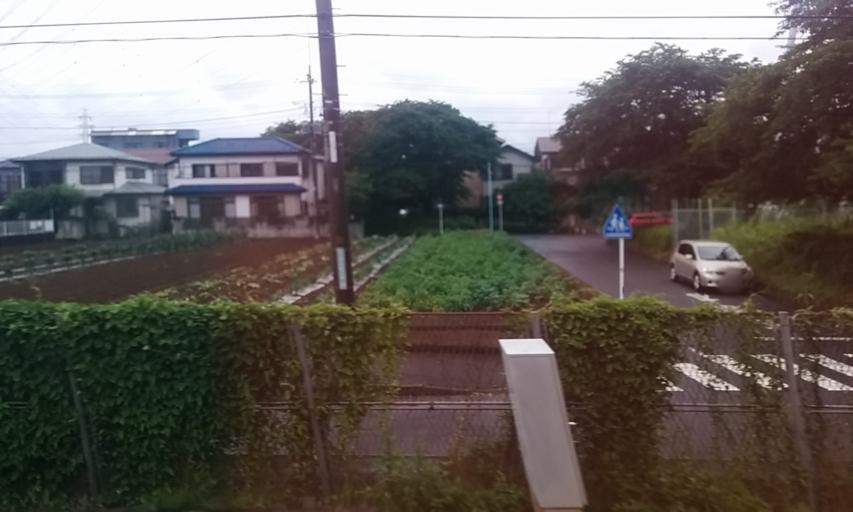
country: JP
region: Tokyo
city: Hino
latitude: 35.6502
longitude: 139.3843
